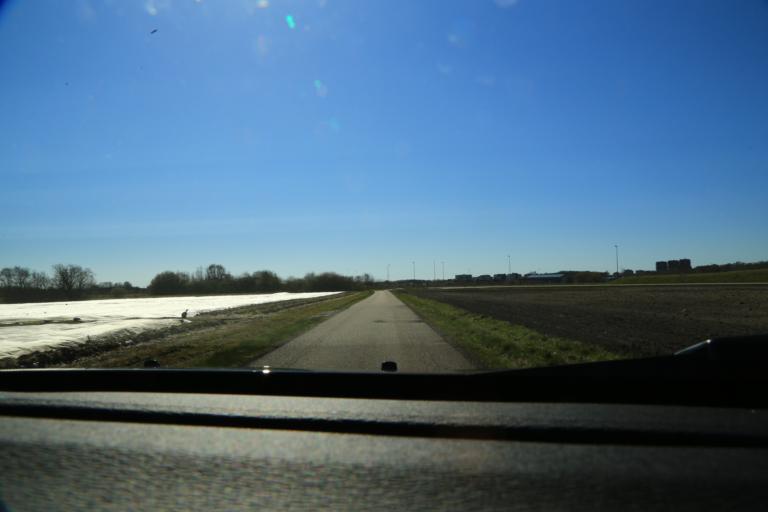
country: SE
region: Halland
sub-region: Varbergs Kommun
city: Traslovslage
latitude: 57.0892
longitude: 12.2926
